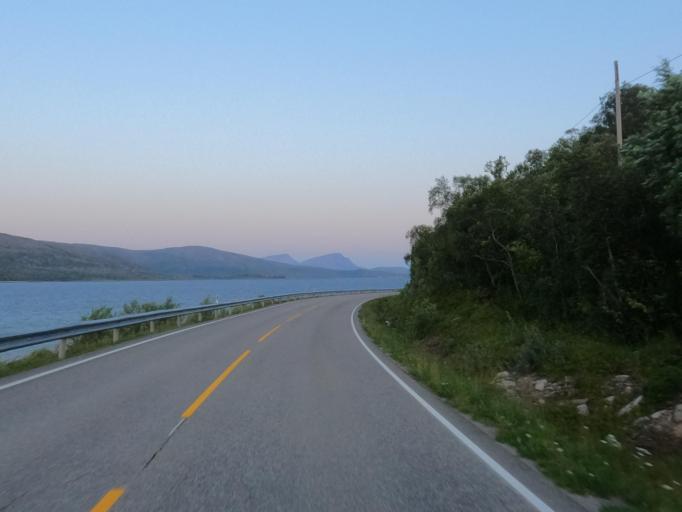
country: NO
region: Nordland
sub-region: Lodingen
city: Lodingen
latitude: 68.4873
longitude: 16.0922
